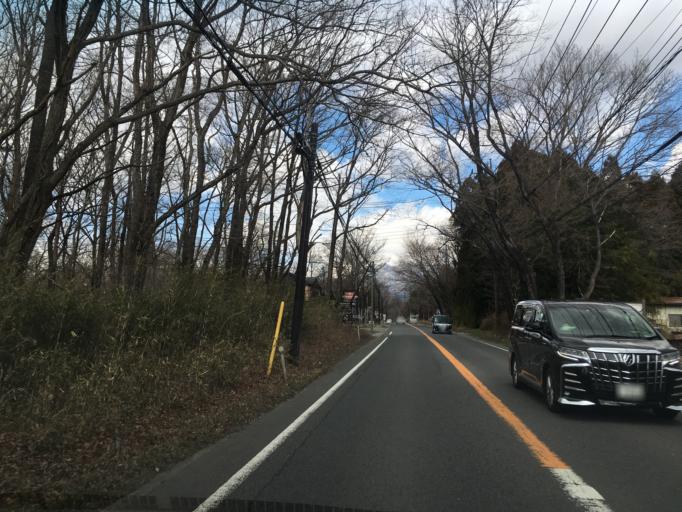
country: JP
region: Tochigi
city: Kuroiso
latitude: 37.0376
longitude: 140.0170
